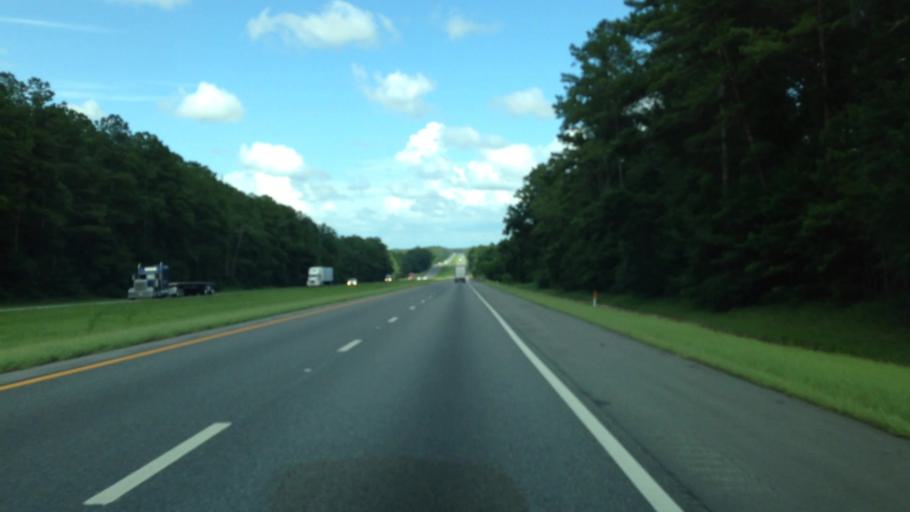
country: US
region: Florida
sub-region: Jefferson County
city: Monticello
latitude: 30.4731
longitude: -83.8663
